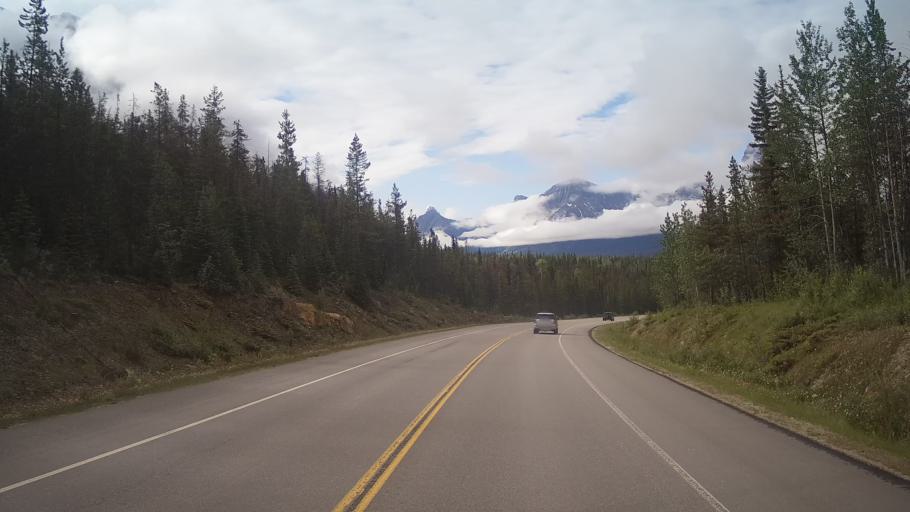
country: CA
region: Alberta
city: Jasper Park Lodge
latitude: 52.6862
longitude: -117.8656
